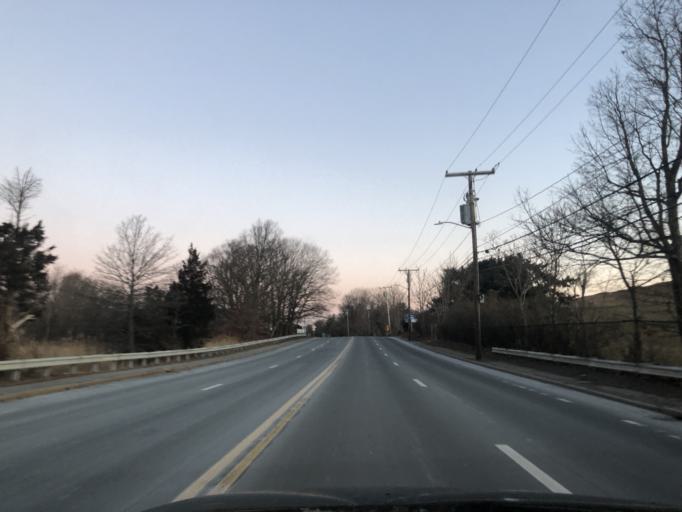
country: US
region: Massachusetts
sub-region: Norfolk County
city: Milton
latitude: 42.2686
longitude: -71.0462
